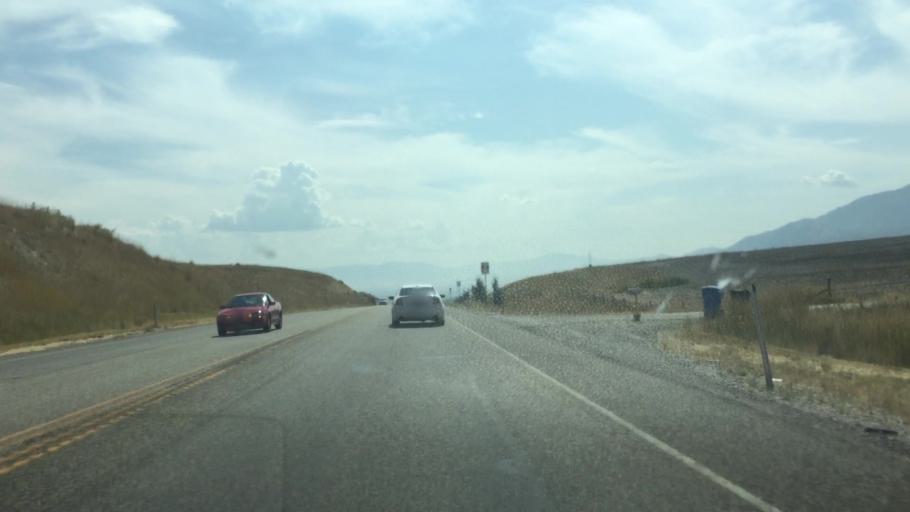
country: US
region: Utah
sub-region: Cache County
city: Mendon
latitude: 41.7708
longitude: -112.0158
